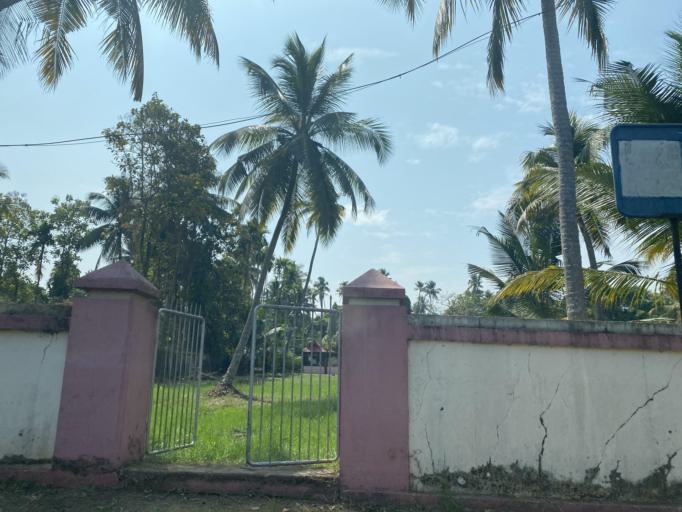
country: IN
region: Kerala
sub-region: Ernakulam
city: Elur
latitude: 10.1082
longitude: 76.2298
